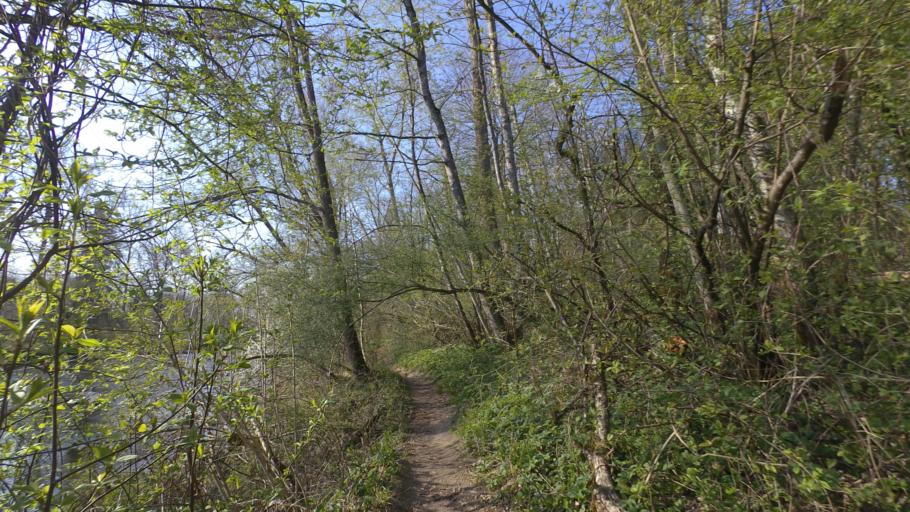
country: DE
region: Bavaria
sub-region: Upper Bavaria
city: Traunreut
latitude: 47.9518
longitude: 12.5856
